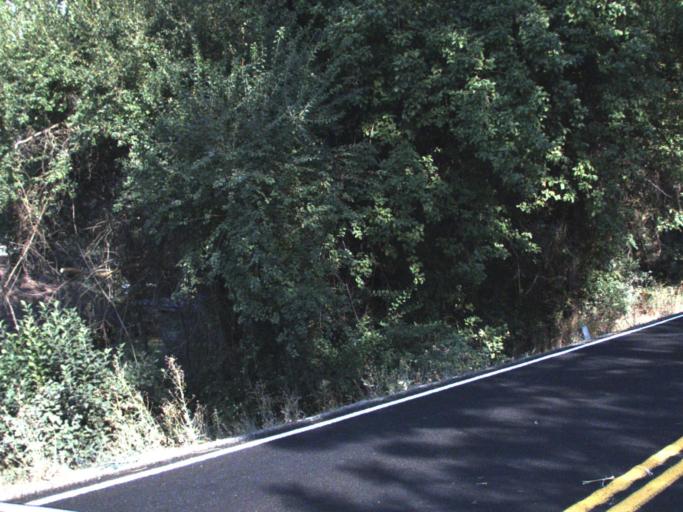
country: US
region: Washington
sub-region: Spokane County
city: Deer Park
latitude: 47.8838
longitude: -117.6576
